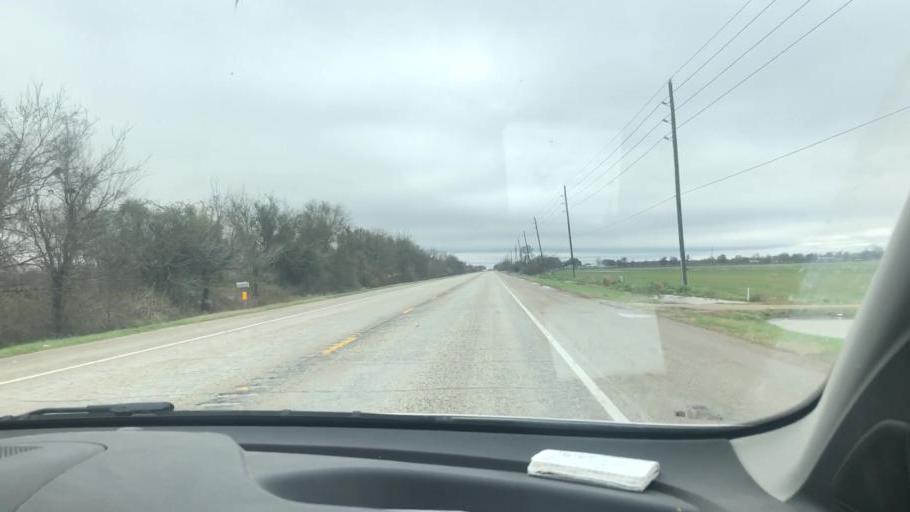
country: US
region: Texas
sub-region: Wharton County
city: Wharton
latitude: 29.2759
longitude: -96.0634
